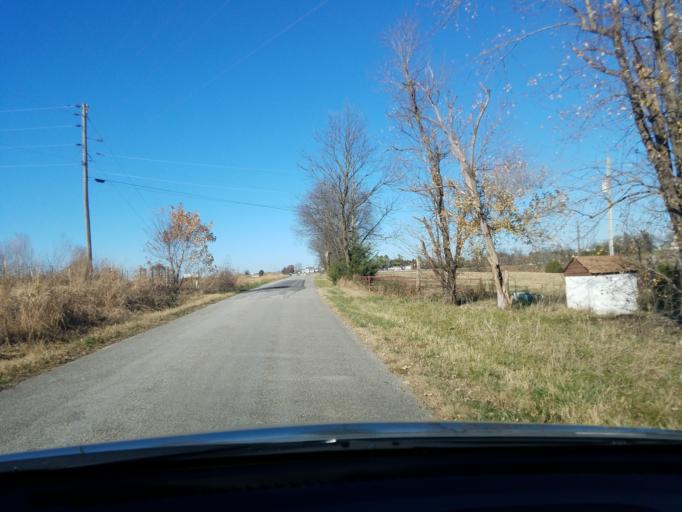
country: US
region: Arkansas
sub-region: Carroll County
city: Berryville
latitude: 36.3851
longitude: -93.6173
